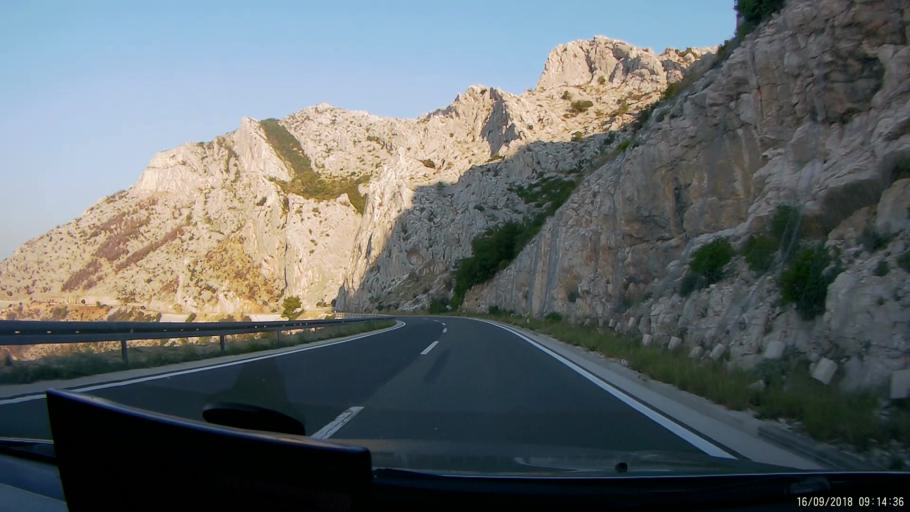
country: HR
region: Splitsko-Dalmatinska
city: Donja Brela
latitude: 43.4037
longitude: 16.8888
